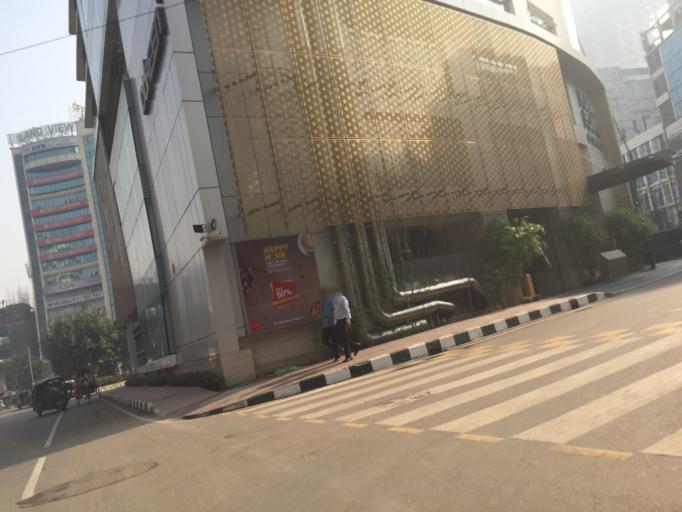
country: BD
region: Dhaka
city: Paltan
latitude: 23.7945
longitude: 90.4134
